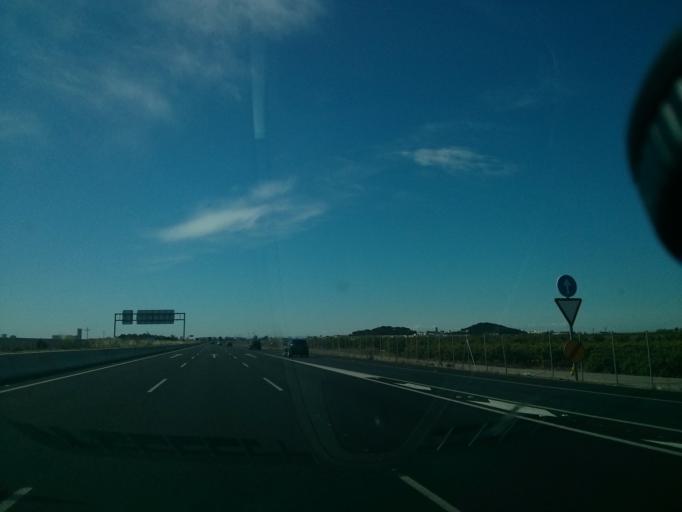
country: ES
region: Valencia
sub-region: Provincia de Valencia
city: Pucol
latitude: 39.6118
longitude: -0.2944
